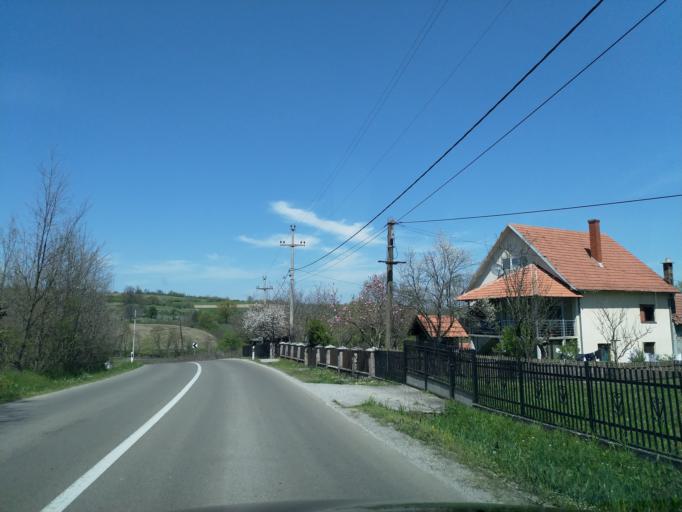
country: RS
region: Central Serbia
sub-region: Belgrade
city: Lazarevac
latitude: 44.3514
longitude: 20.3786
